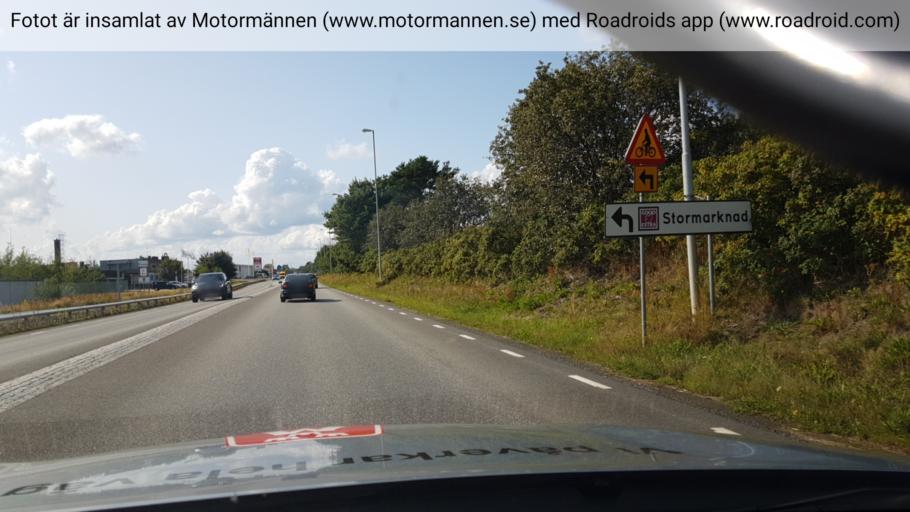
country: SE
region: Skane
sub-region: Hassleholms Kommun
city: Hassleholm
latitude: 56.1480
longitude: 13.7878
